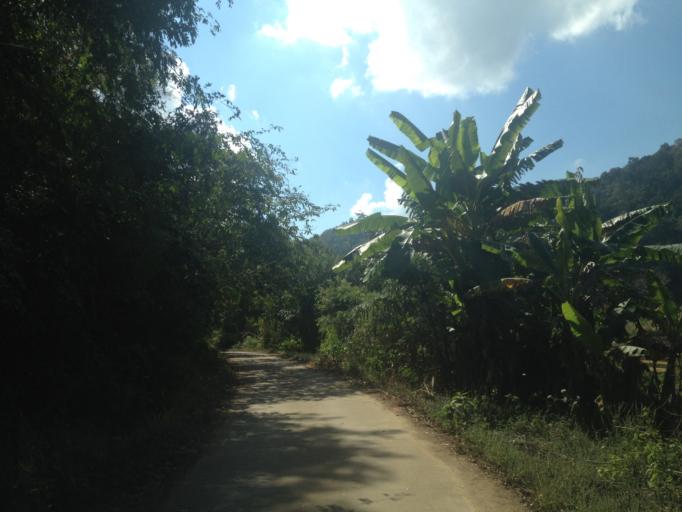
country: TH
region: Mae Hong Son
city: Ban Huai I Huak
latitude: 18.1005
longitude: 98.1891
